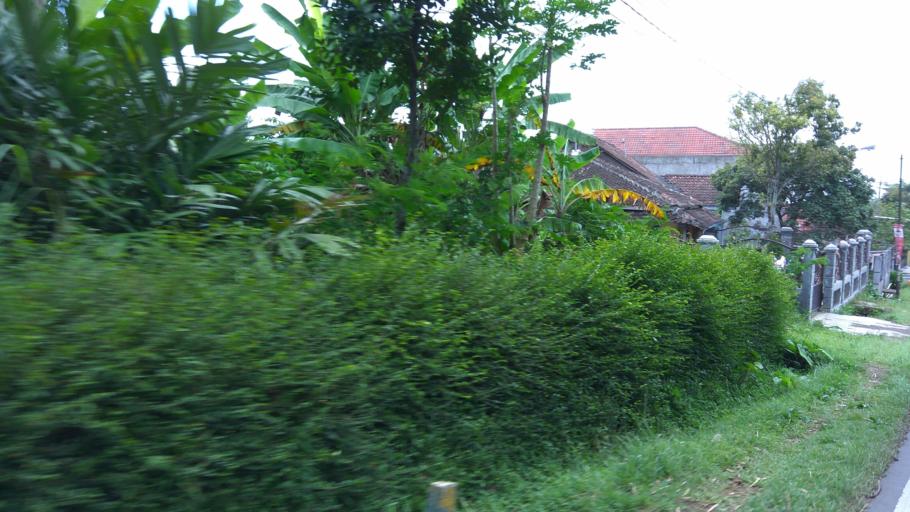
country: ID
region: Central Java
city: Ambarawa
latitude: -7.2403
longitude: 110.3901
